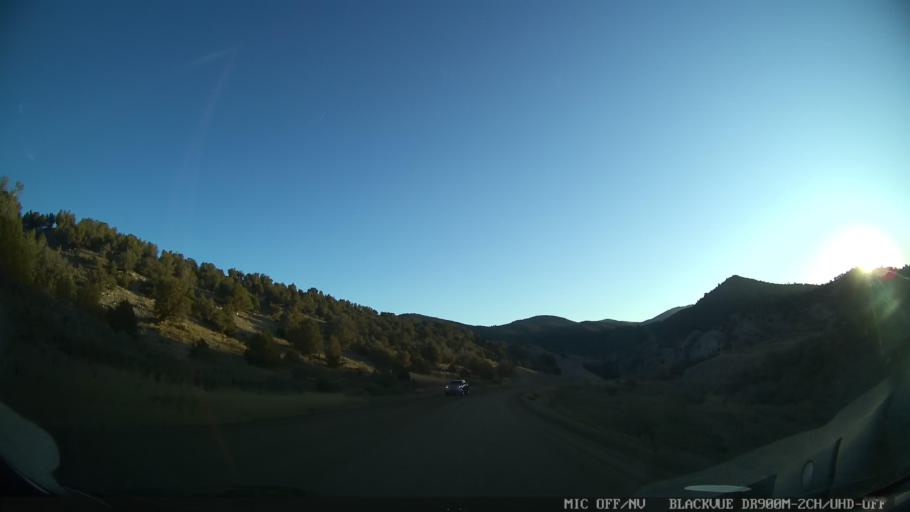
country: US
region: Colorado
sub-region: Grand County
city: Kremmling
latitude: 39.9249
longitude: -106.5343
